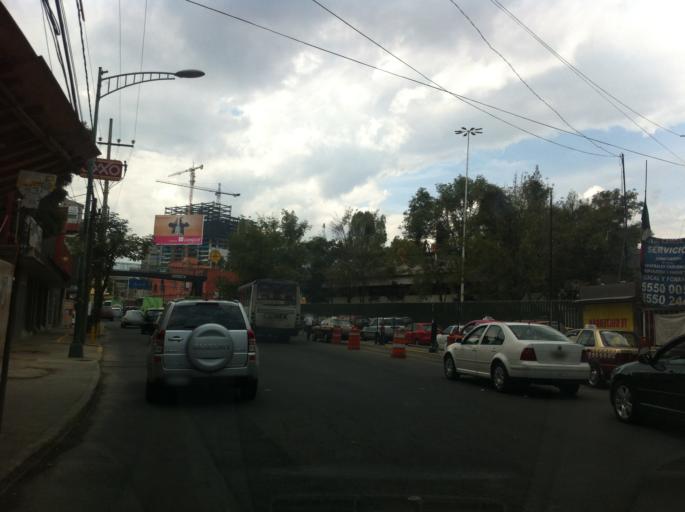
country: MX
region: Mexico City
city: Magdalena Contreras
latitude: 19.3363
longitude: -99.2006
